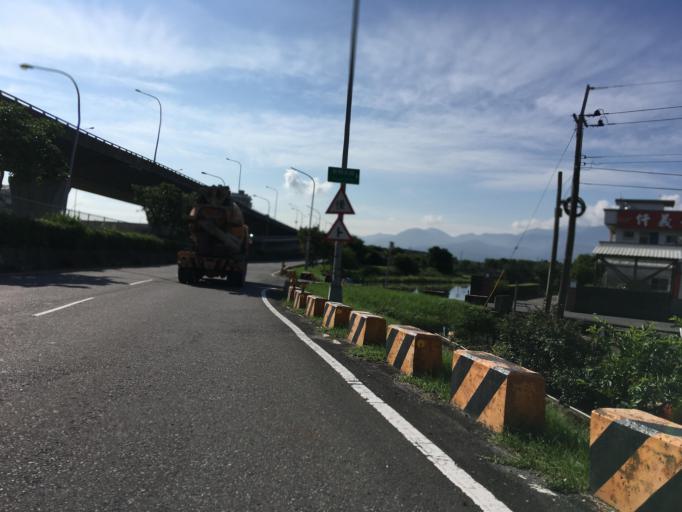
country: TW
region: Taiwan
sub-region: Yilan
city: Yilan
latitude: 24.6752
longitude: 121.7943
